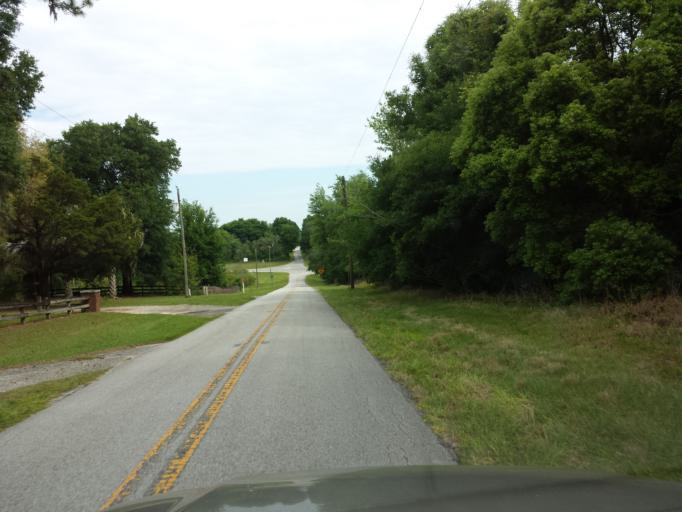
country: US
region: Florida
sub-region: Pasco County
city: San Antonio
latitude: 28.4173
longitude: -82.2783
